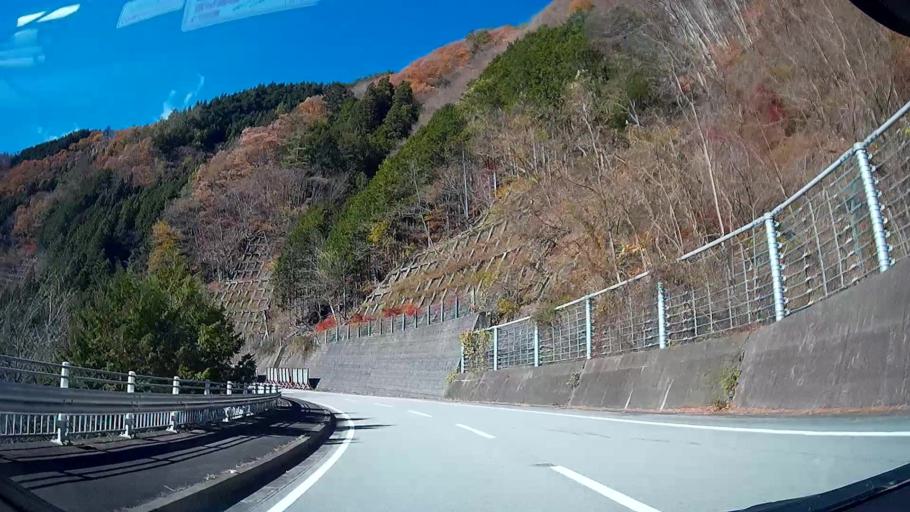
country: JP
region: Yamanashi
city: Otsuki
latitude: 35.7605
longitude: 138.9685
